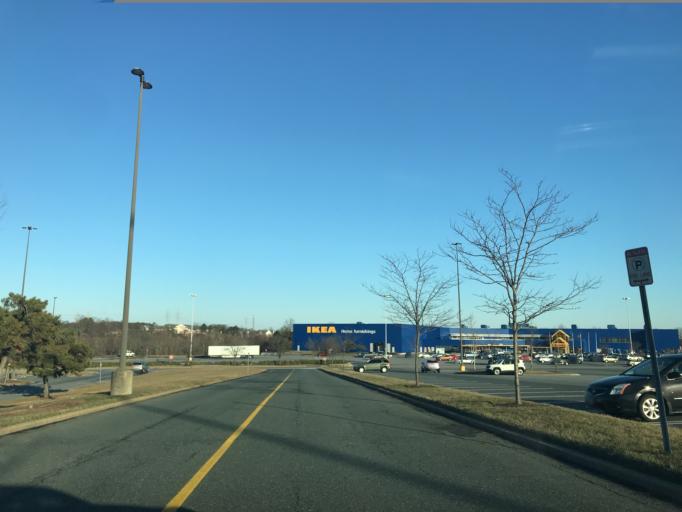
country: US
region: Maryland
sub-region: Baltimore County
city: White Marsh
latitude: 39.3757
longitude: -76.4653
